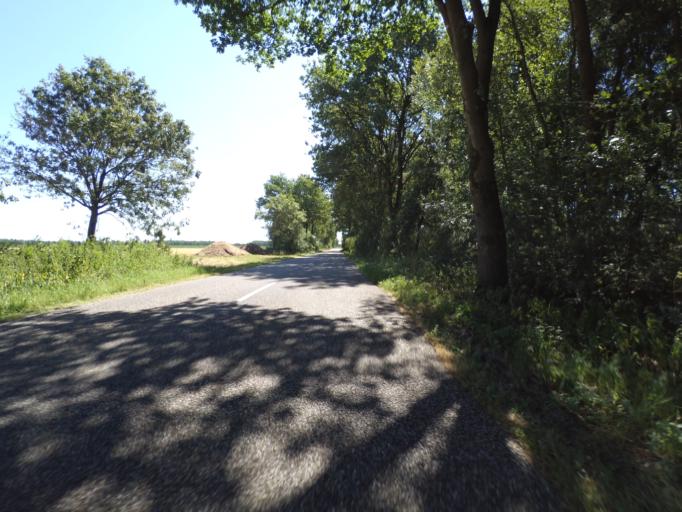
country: NL
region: Drenthe
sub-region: Gemeente Coevorden
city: Sleen
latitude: 52.8370
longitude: 6.6794
